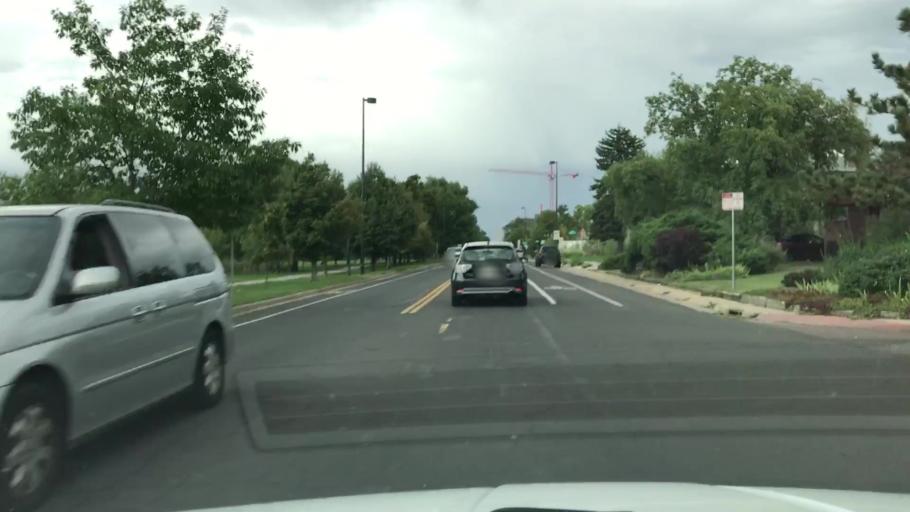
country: US
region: Colorado
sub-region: Jefferson County
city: Edgewater
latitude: 39.7439
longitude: -105.0510
